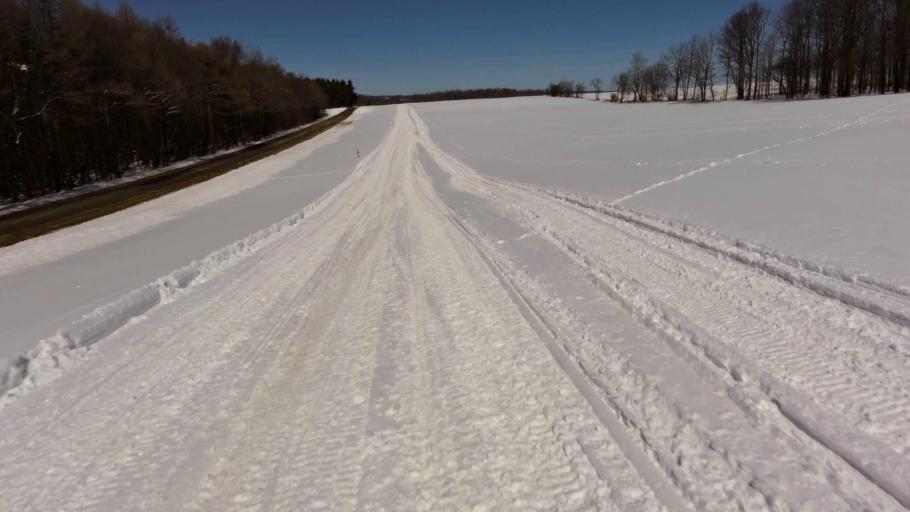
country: US
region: New York
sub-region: Allegany County
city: Houghton
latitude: 42.3525
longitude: -78.2605
